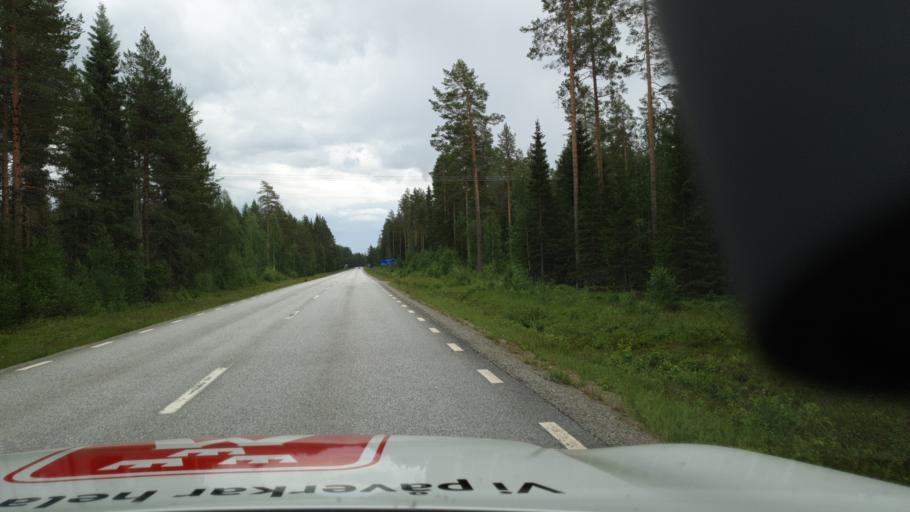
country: SE
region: Vaesterbotten
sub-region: Vindelns Kommun
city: Vindeln
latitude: 64.0886
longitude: 19.6191
